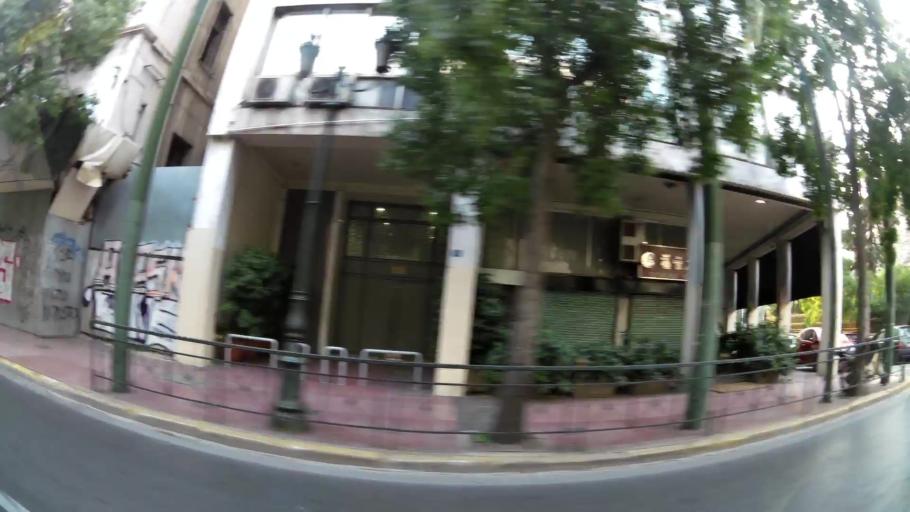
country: GR
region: Attica
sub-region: Nomarchia Athinas
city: Athens
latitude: 37.9726
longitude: 23.7336
